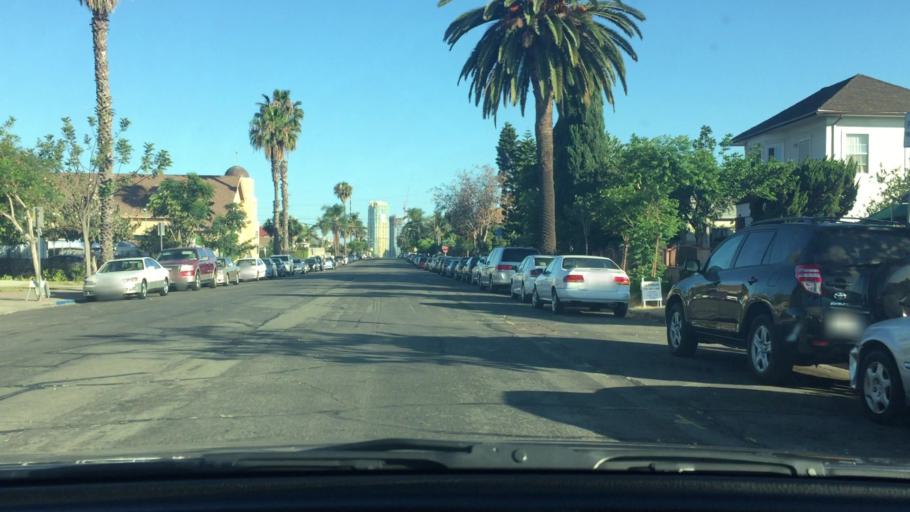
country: US
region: California
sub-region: San Diego County
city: San Diego
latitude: 32.6986
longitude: -117.1343
